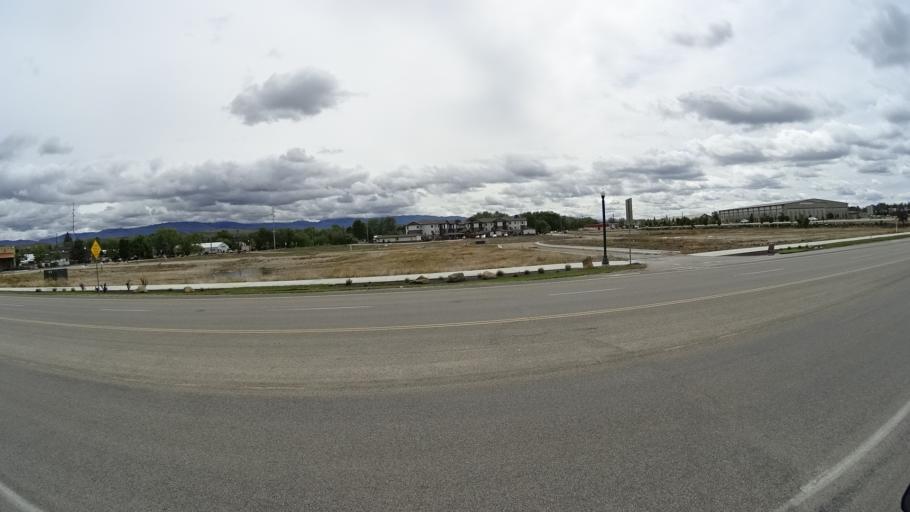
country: US
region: Idaho
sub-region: Ada County
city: Eagle
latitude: 43.6889
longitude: -116.3341
